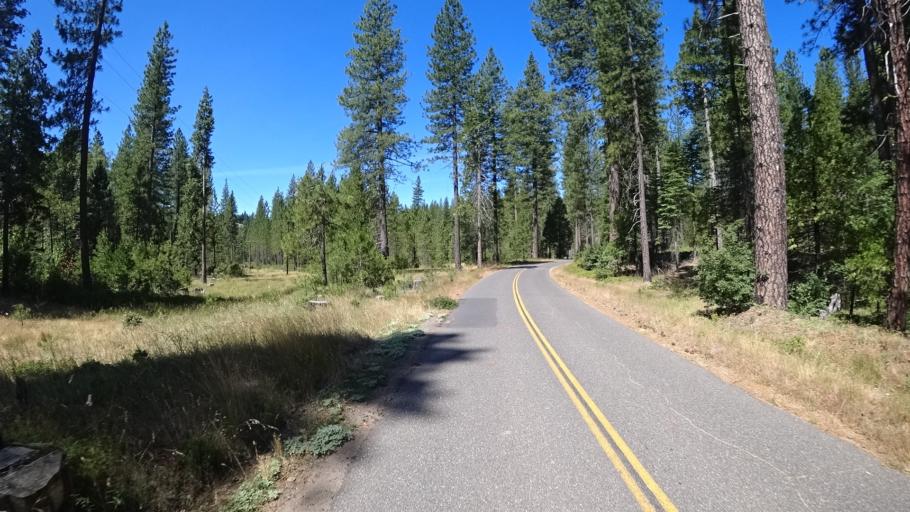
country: US
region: California
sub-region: Amador County
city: Pioneer
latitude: 38.4344
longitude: -120.4450
